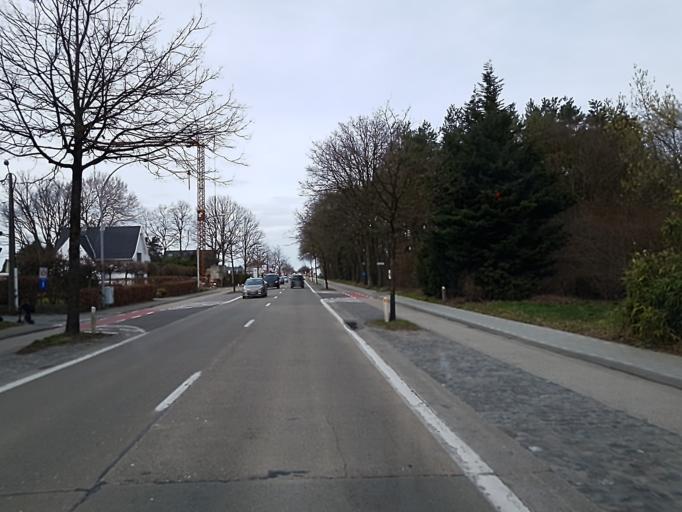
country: BE
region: Flanders
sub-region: Provincie Antwerpen
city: Mol
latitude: 51.2009
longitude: 5.1156
